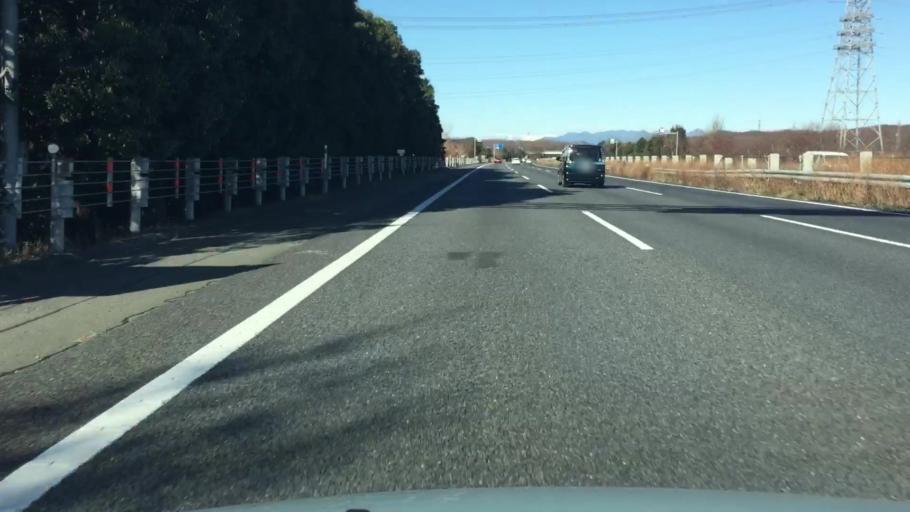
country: JP
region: Saitama
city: Honjo
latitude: 36.2023
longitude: 139.1790
